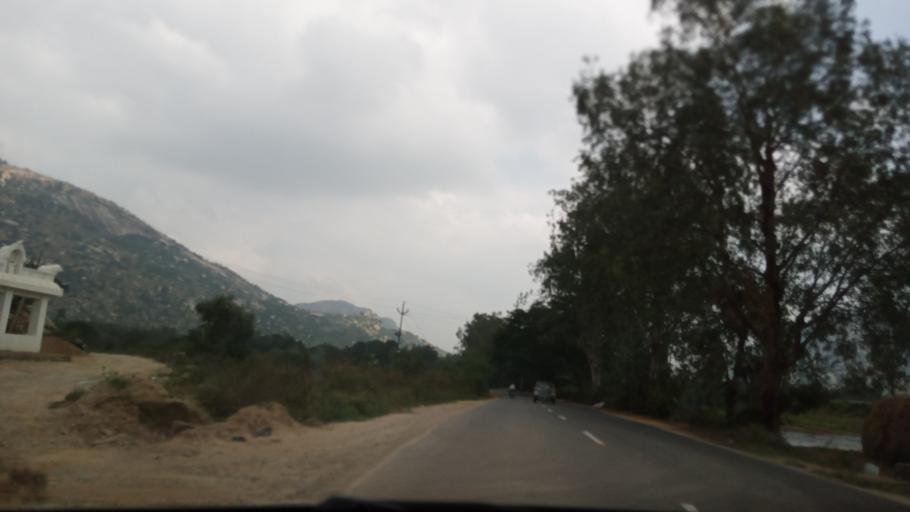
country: IN
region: Andhra Pradesh
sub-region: Chittoor
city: Madanapalle
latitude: 13.6368
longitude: 78.5797
